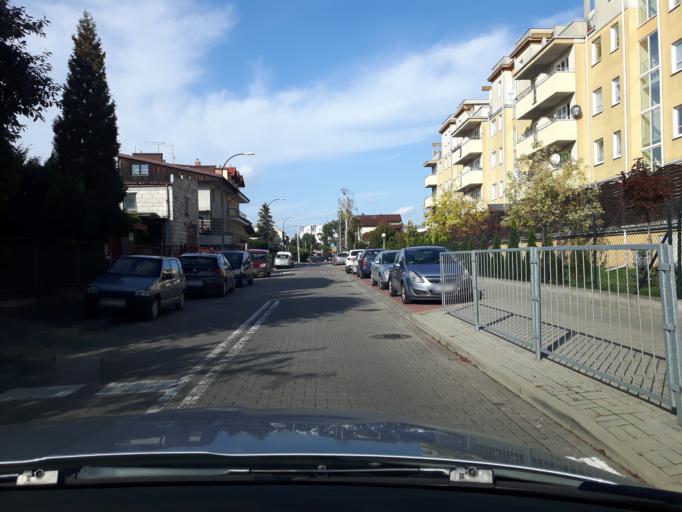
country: PL
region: Masovian Voivodeship
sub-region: Powiat wolominski
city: Zabki
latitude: 52.2840
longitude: 21.0808
